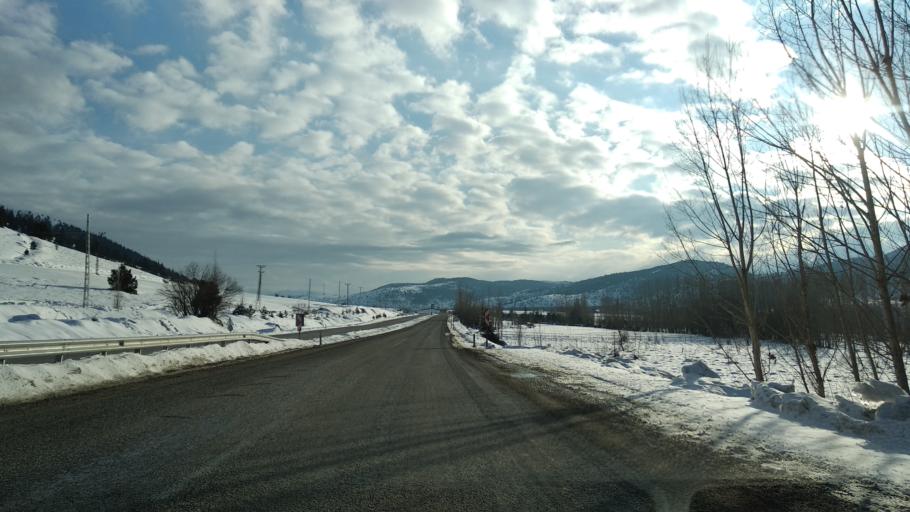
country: TR
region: Kahramanmaras
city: Goksun
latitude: 38.0903
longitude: 36.4695
